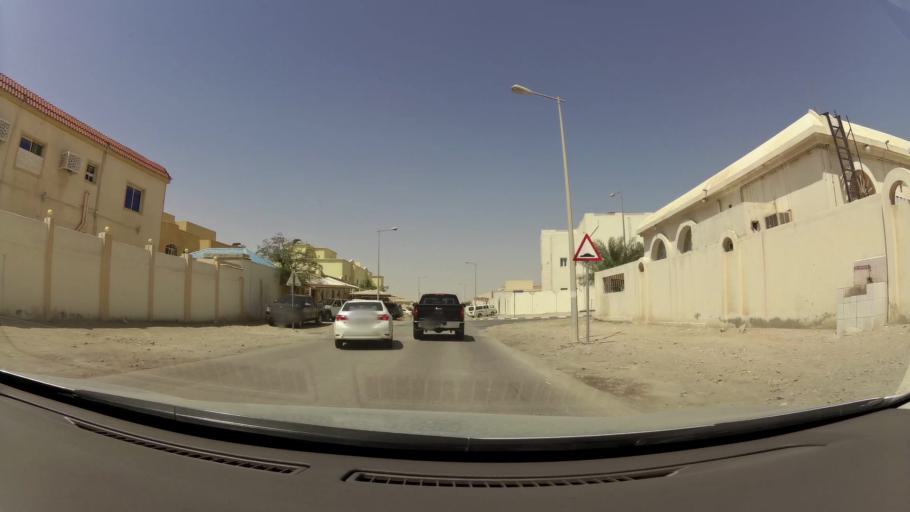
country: QA
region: Baladiyat ar Rayyan
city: Ar Rayyan
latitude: 25.2607
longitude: 51.4120
